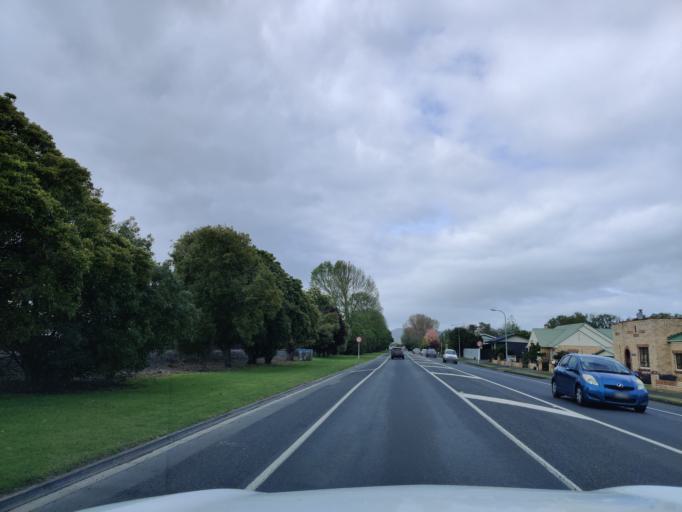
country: NZ
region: Waikato
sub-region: Waikato District
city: Ngaruawahia
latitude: -37.5436
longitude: 175.1583
